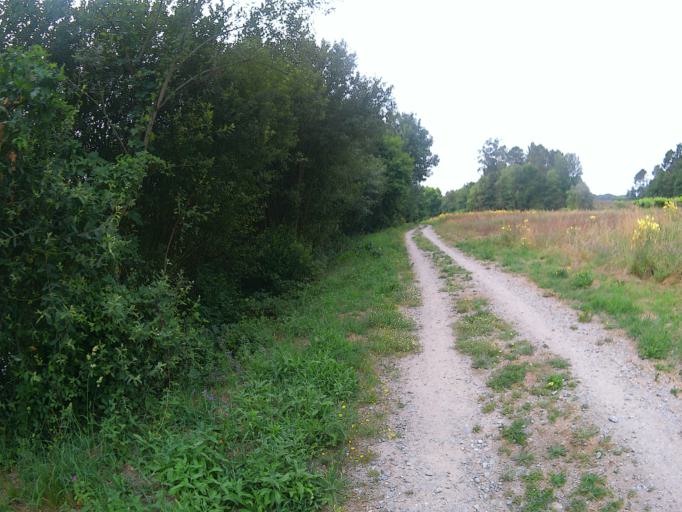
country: PT
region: Viana do Castelo
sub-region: Ponte de Lima
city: Ponte de Lima
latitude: 41.7896
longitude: -8.5153
